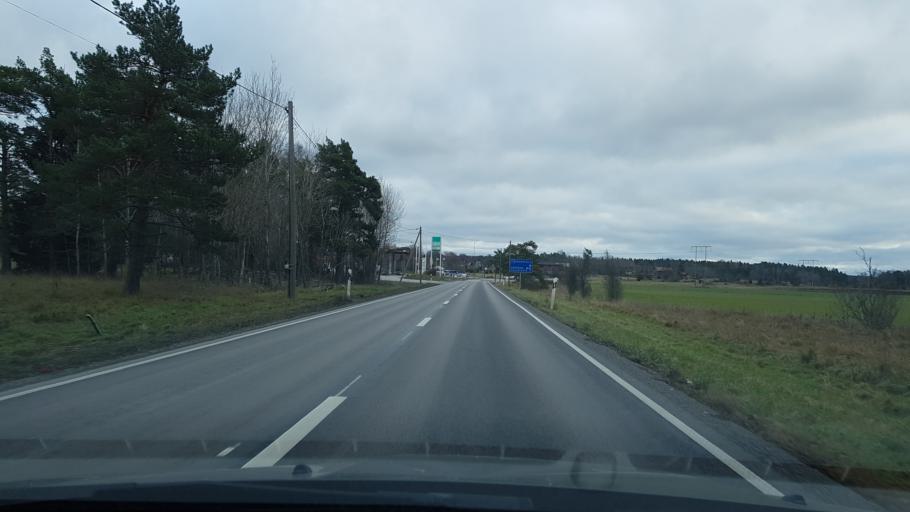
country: SE
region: Stockholm
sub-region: Norrtalje Kommun
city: Hallstavik
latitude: 60.0416
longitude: 18.5482
